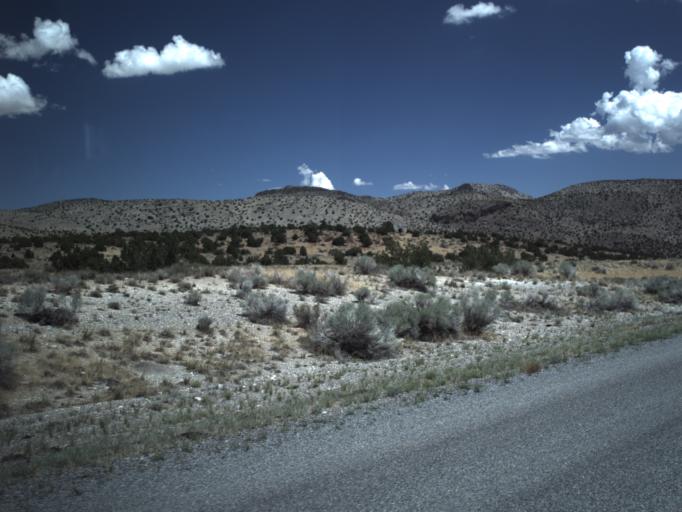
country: US
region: Utah
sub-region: Beaver County
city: Milford
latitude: 39.0776
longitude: -113.6195
